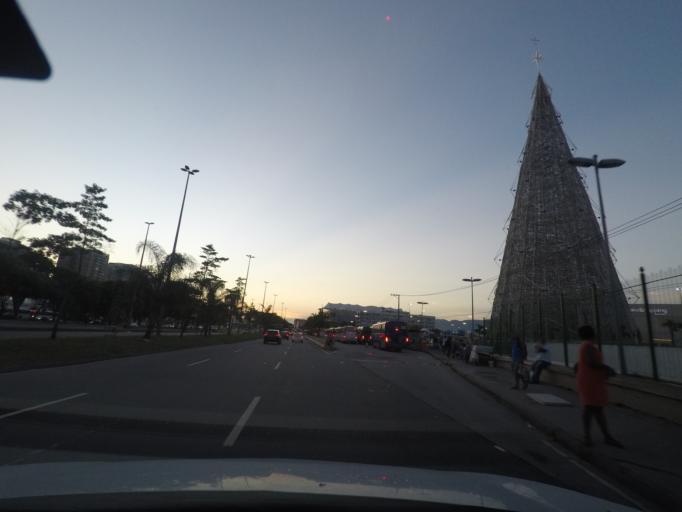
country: BR
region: Rio de Janeiro
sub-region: Rio De Janeiro
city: Rio de Janeiro
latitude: -22.9995
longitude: -43.3566
